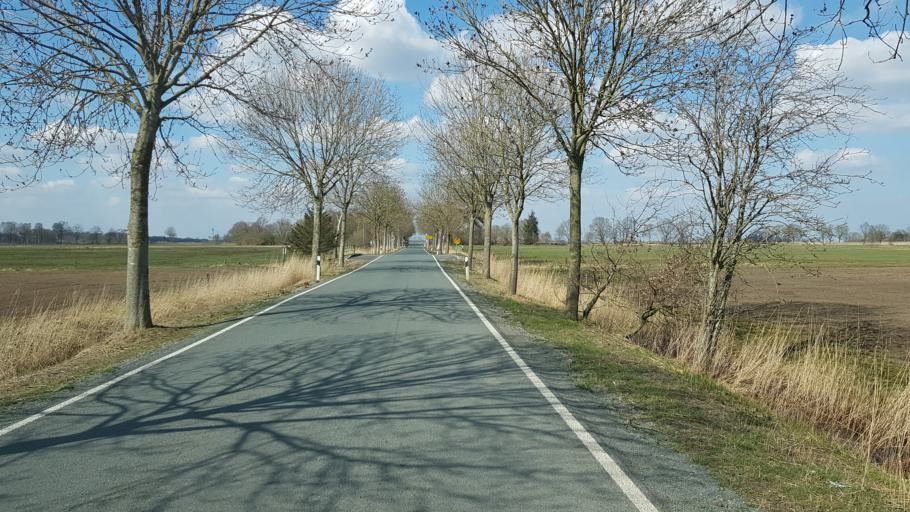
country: DE
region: Lower Saxony
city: Rastede
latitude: 53.3359
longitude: 8.2230
